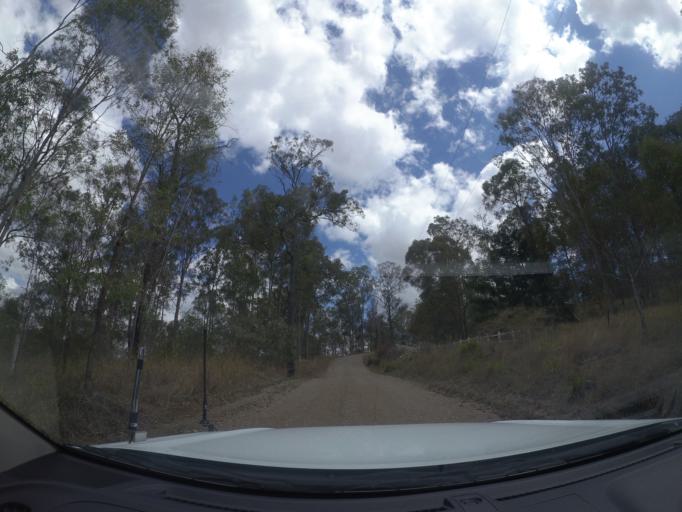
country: AU
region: Queensland
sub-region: Logan
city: Cedar Vale
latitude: -27.9001
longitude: 153.0005
